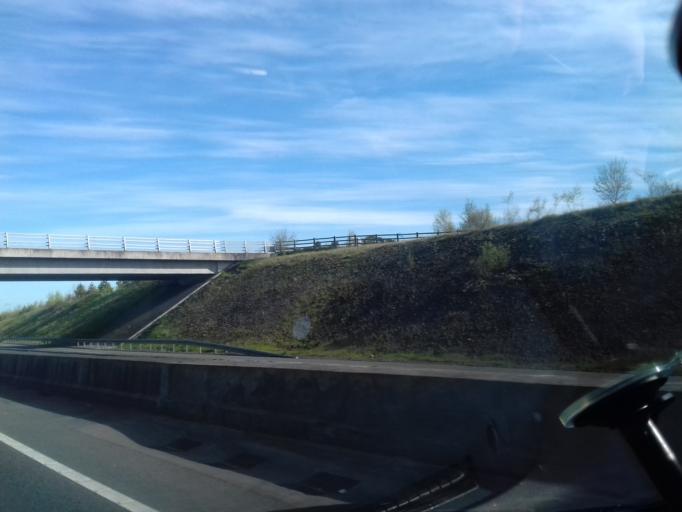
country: IE
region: Leinster
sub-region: An Mhi
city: Dunshaughlin
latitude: 53.5695
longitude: -6.5725
